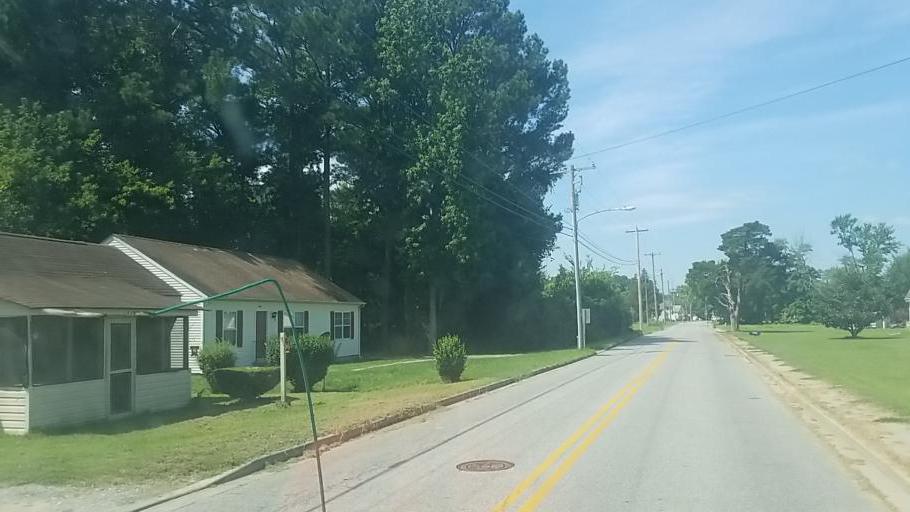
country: US
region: Maryland
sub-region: Caroline County
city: Denton
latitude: 38.8835
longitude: -75.8182
